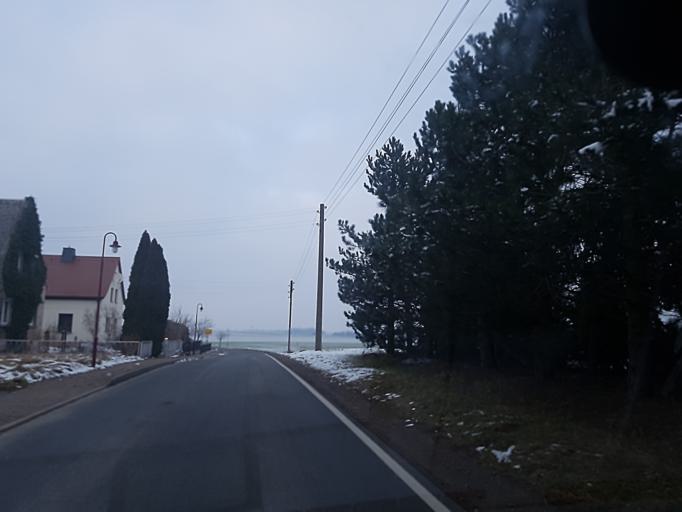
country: DE
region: Saxony
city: Naundorf
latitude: 51.2603
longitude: 13.1041
